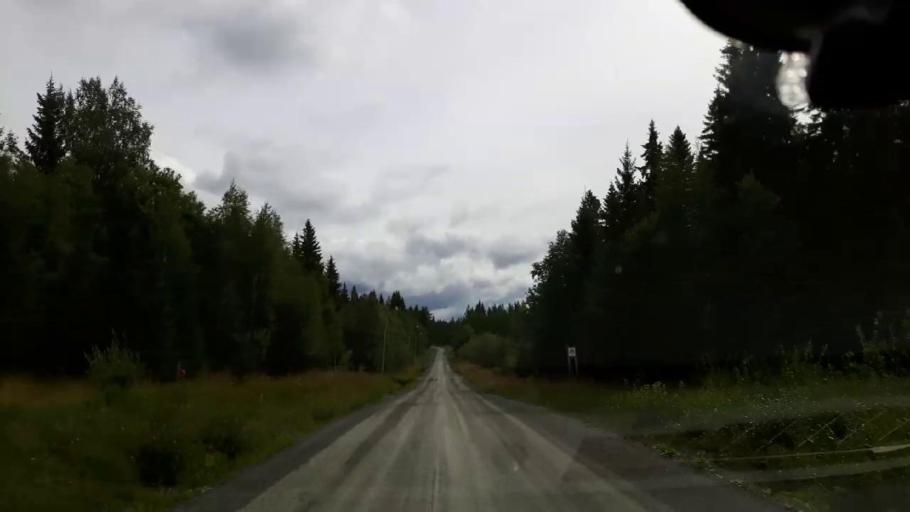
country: SE
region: Jaemtland
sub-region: Krokoms Kommun
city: Valla
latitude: 63.6435
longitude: 13.9931
